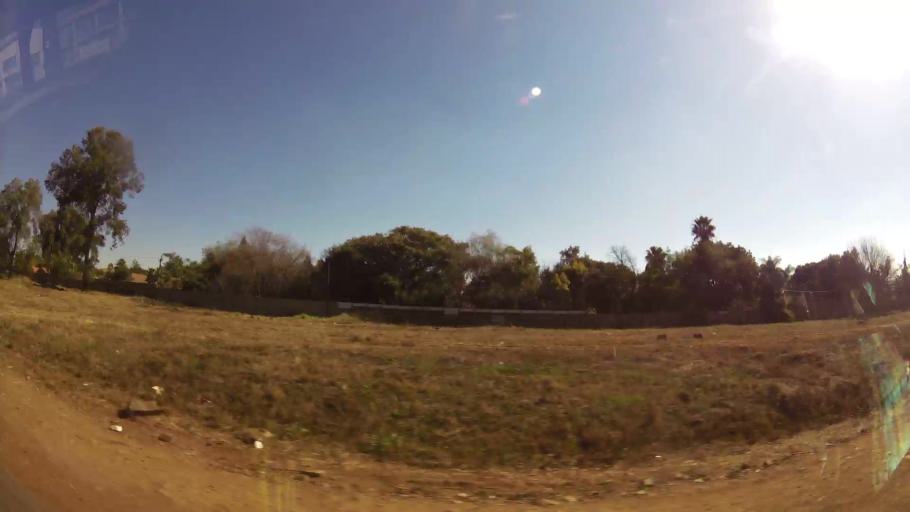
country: ZA
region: Gauteng
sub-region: City of Tshwane Metropolitan Municipality
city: Centurion
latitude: -25.8683
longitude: 28.1624
